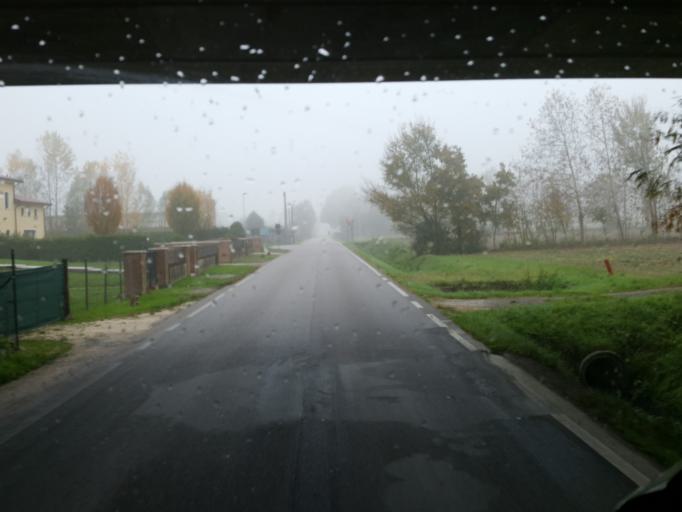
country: IT
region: Veneto
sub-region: Provincia di Padova
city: Borgoricco-San Michele delle Badesse-Sant'Eufemia
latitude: 45.5411
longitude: 11.9460
